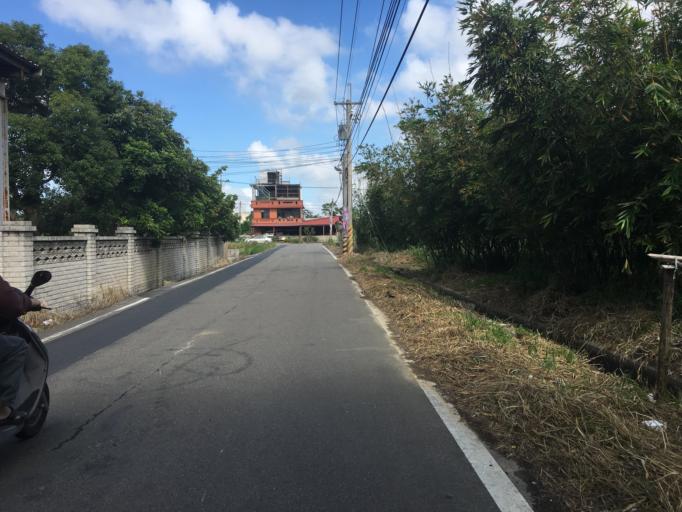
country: TW
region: Taiwan
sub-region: Hsinchu
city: Zhubei
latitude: 24.8878
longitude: 121.0485
